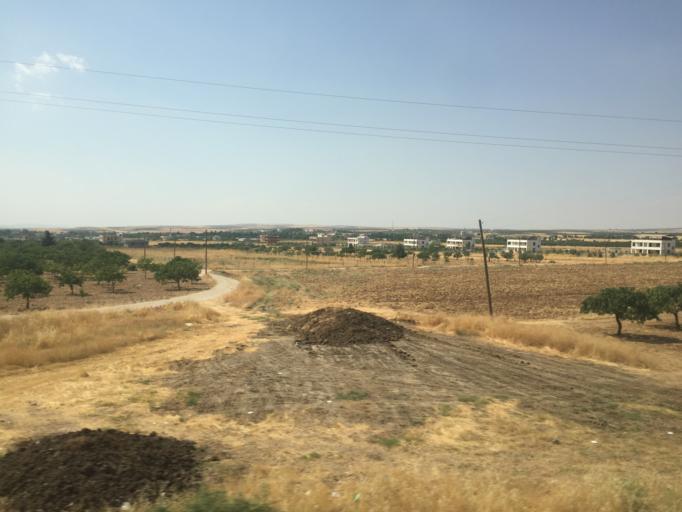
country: TR
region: Sanliurfa
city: Akziyaret
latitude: 37.3458
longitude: 38.8114
